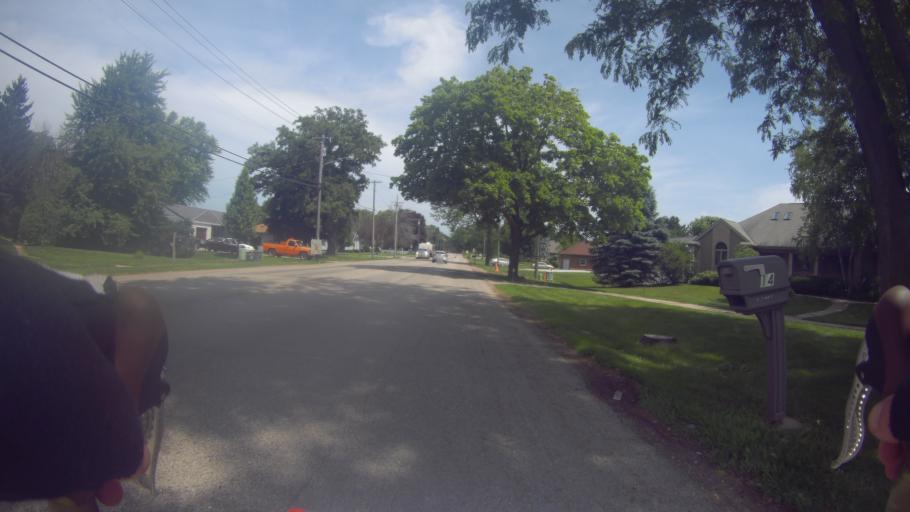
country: US
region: Wisconsin
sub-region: Jefferson County
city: Lake Mills
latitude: 43.0667
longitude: -88.9138
